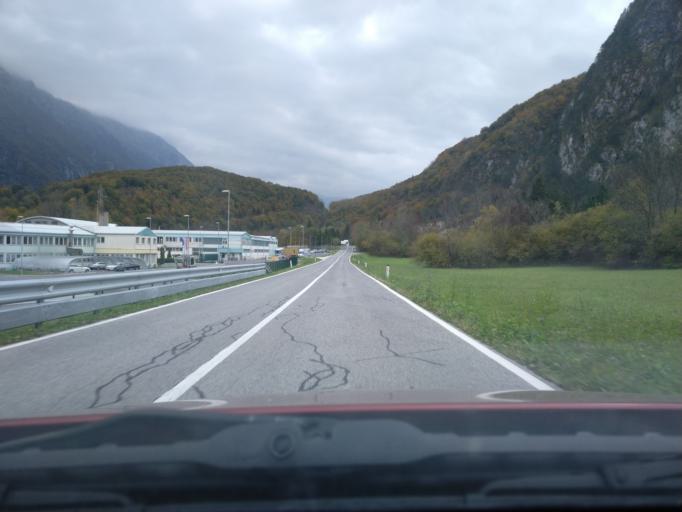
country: SI
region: Bovec
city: Bovec
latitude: 46.2841
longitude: 13.5148
